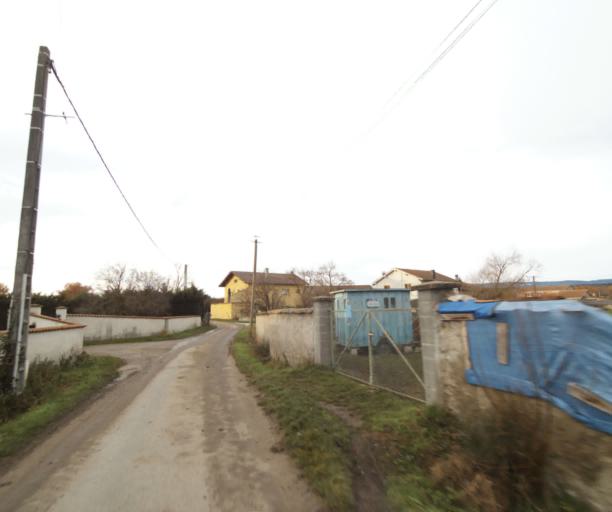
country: FR
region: Rhone-Alpes
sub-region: Departement de la Loire
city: Sury-le-Comtal
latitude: 45.5271
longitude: 4.1646
